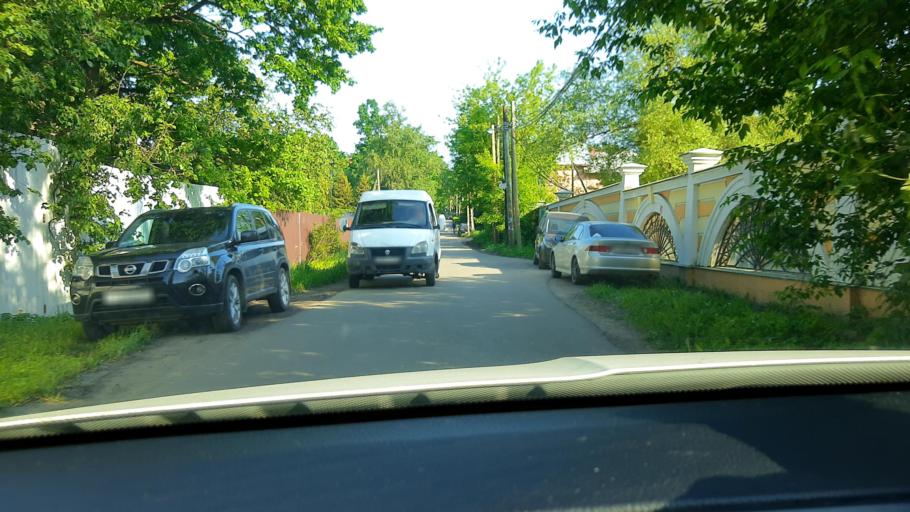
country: RU
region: Moscow
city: Mikhalkovo
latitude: 55.6770
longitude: 37.4160
